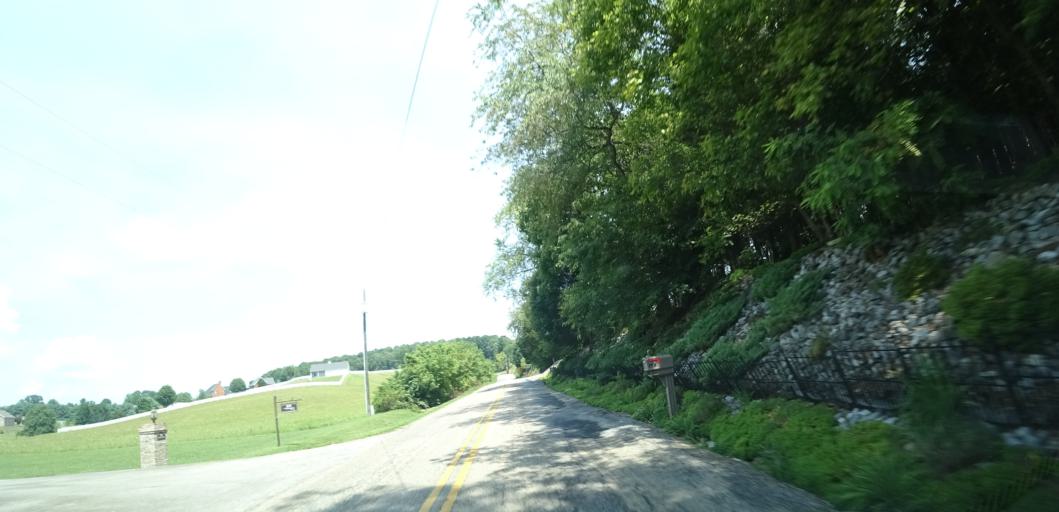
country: US
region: Virginia
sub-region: Botetourt County
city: Fincastle
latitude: 37.4710
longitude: -79.8442
